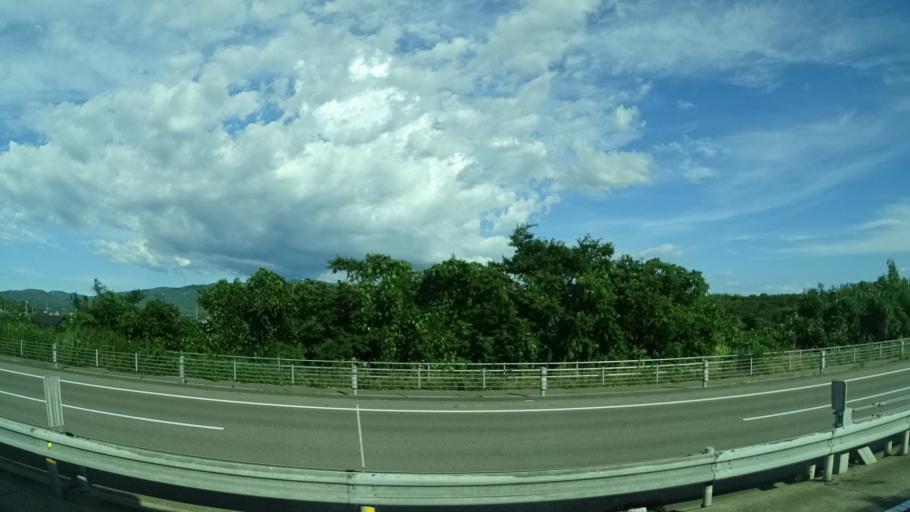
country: JP
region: Ishikawa
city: Hakui
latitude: 36.7978
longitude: 136.7328
